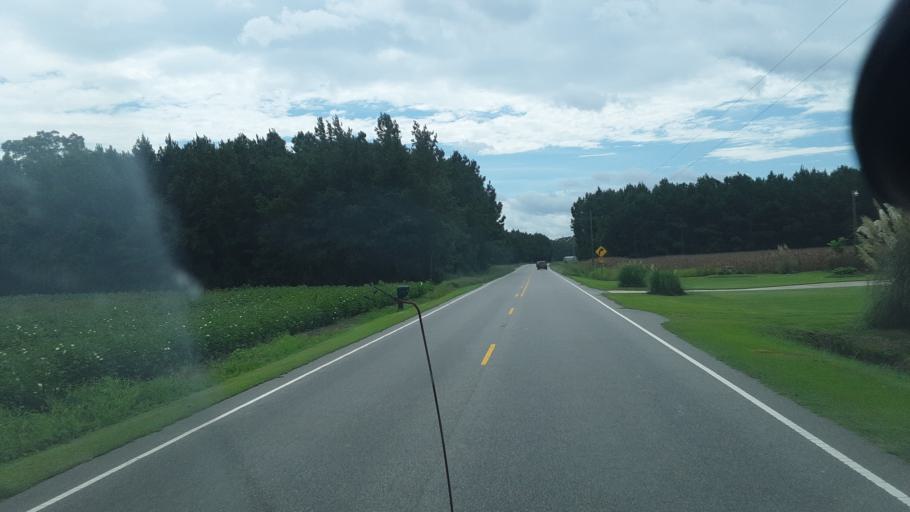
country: US
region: North Carolina
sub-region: Robeson County
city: Rowland
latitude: 34.6270
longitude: -79.3367
